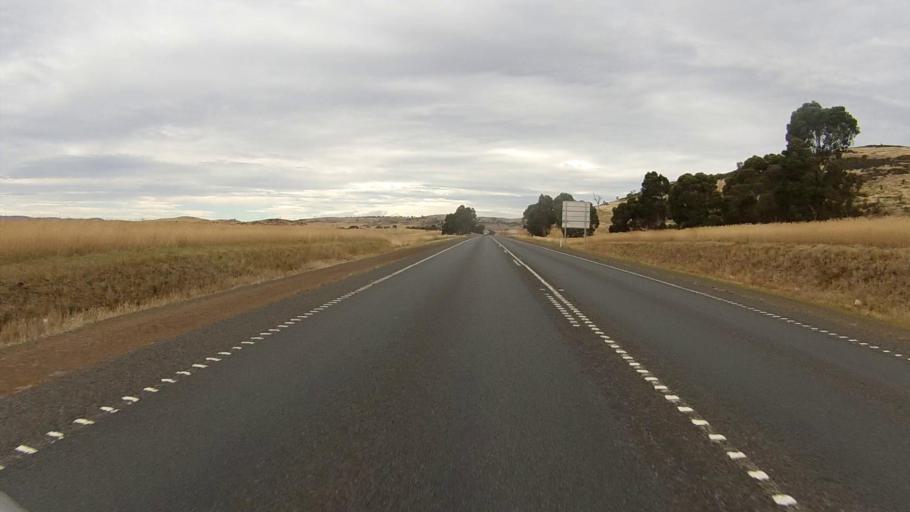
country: AU
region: Tasmania
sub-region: Brighton
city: Bridgewater
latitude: -42.3806
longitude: 147.3203
